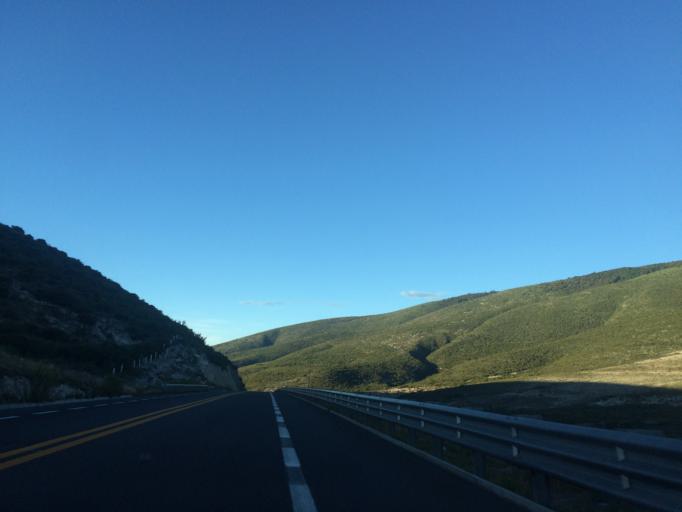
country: MX
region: Puebla
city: Morelos Canada
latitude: 18.6807
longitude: -97.4602
